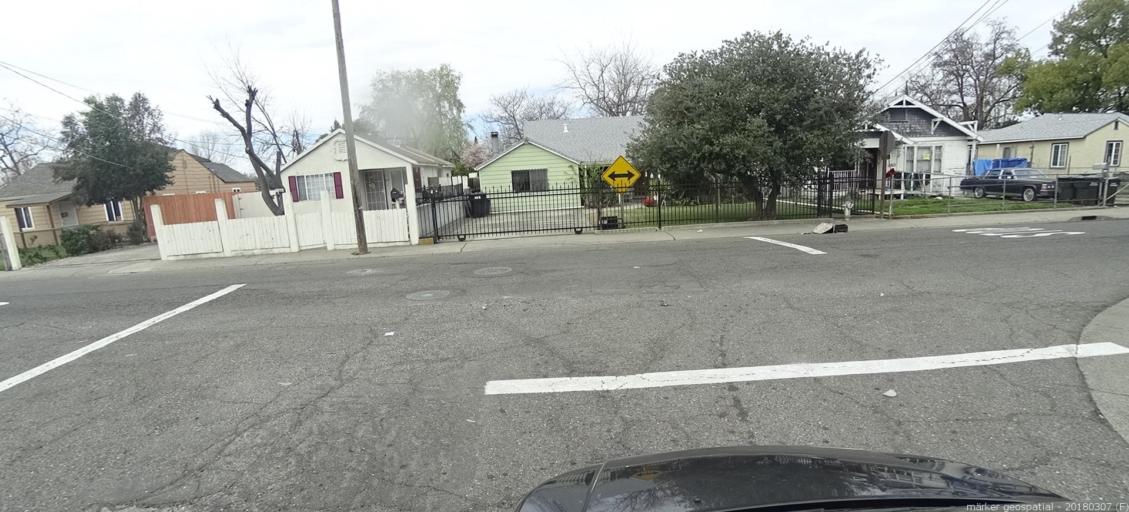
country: US
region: California
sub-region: Sacramento County
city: Parkway
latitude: 38.5283
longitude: -121.4614
